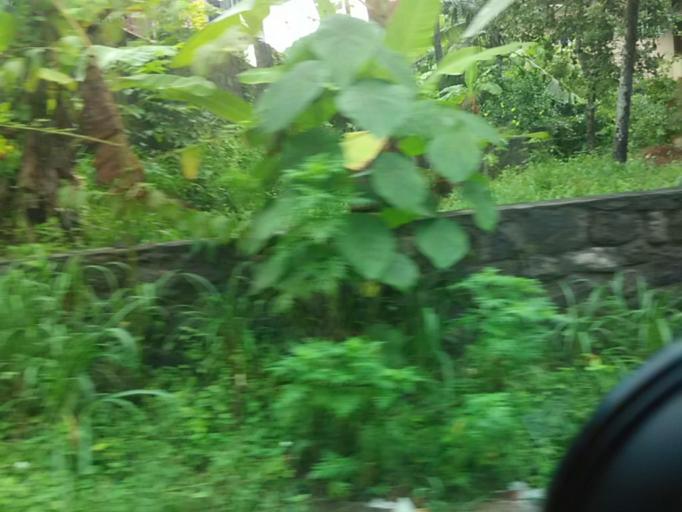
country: IN
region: Kerala
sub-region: Kozhikode
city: Kozhikode
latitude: 11.2795
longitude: 75.8082
